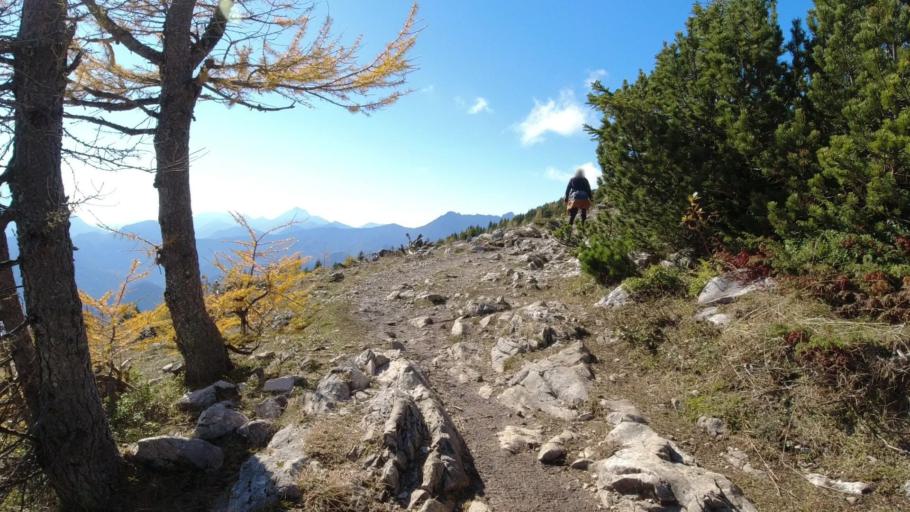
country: AT
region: Carinthia
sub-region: Politischer Bezirk Volkermarkt
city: Gallizien
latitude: 46.5022
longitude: 14.4966
